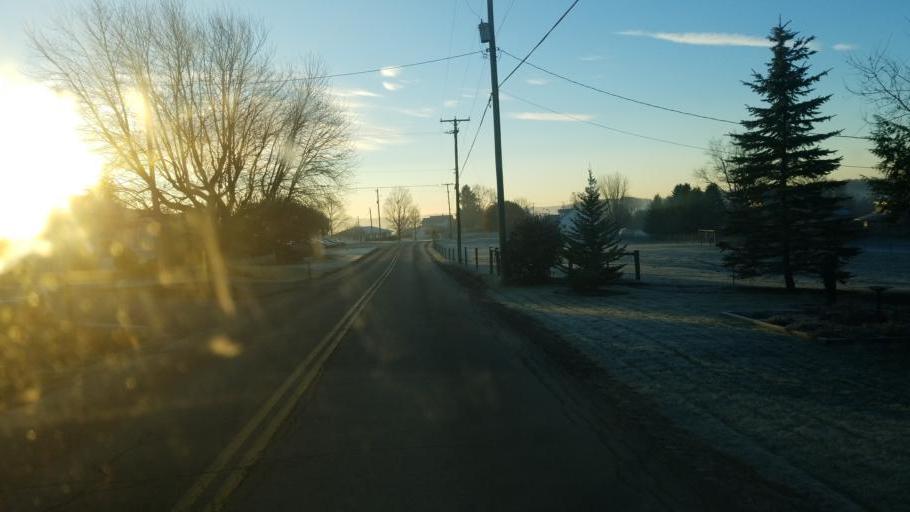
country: US
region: Ohio
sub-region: Holmes County
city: Millersburg
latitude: 40.6179
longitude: -81.8269
